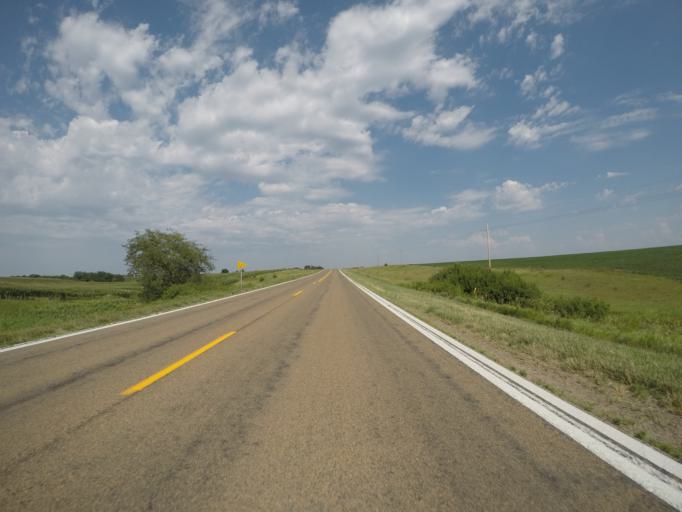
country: US
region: Nebraska
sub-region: Thayer County
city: Hebron
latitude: 40.0165
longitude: -97.5795
